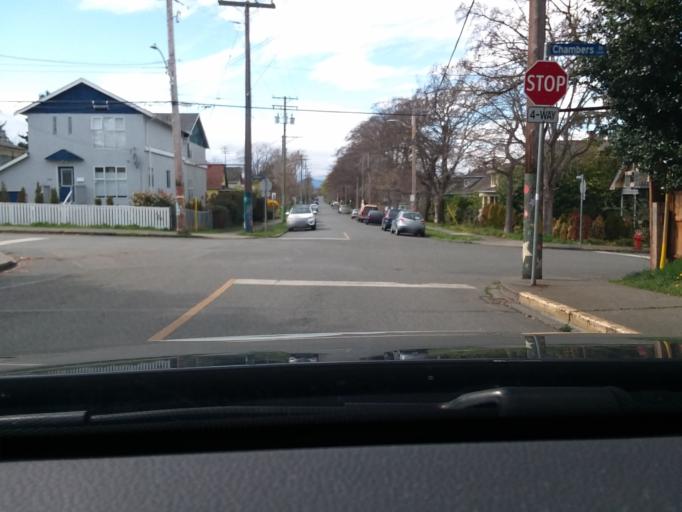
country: CA
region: British Columbia
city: Victoria
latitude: 48.4317
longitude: -123.3495
